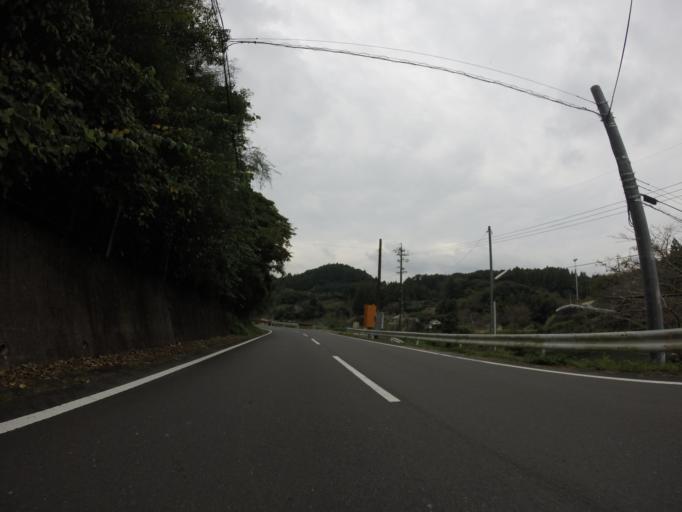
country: JP
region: Shizuoka
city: Kakegawa
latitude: 34.8238
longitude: 138.0145
